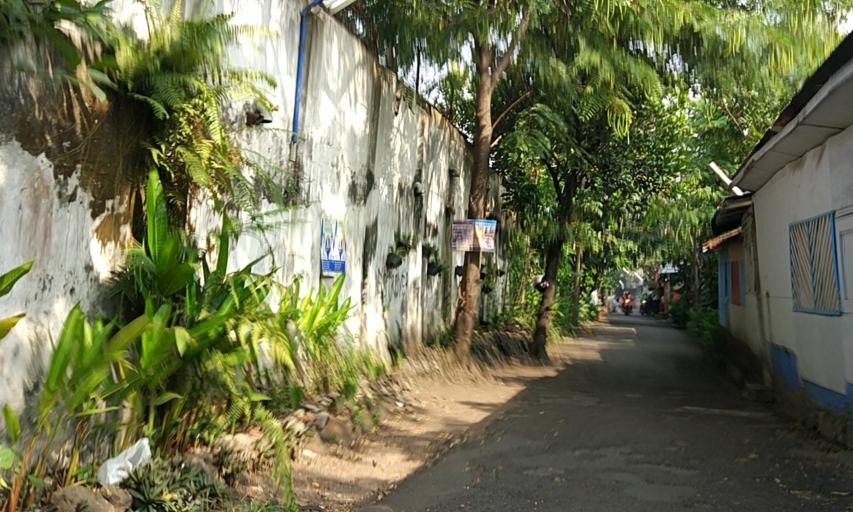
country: ID
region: West Java
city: Bandung
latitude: -6.9034
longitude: 107.6493
